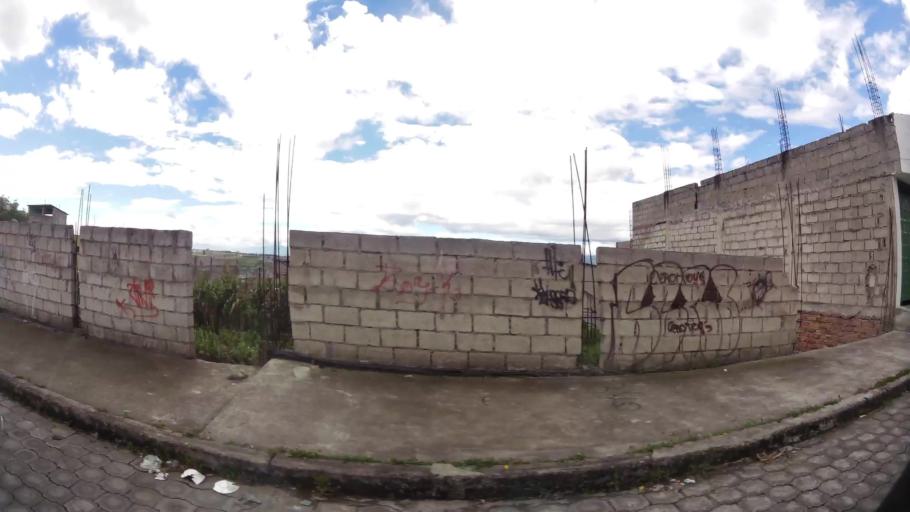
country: EC
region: Pichincha
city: Sangolqui
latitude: -0.3414
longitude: -78.5577
